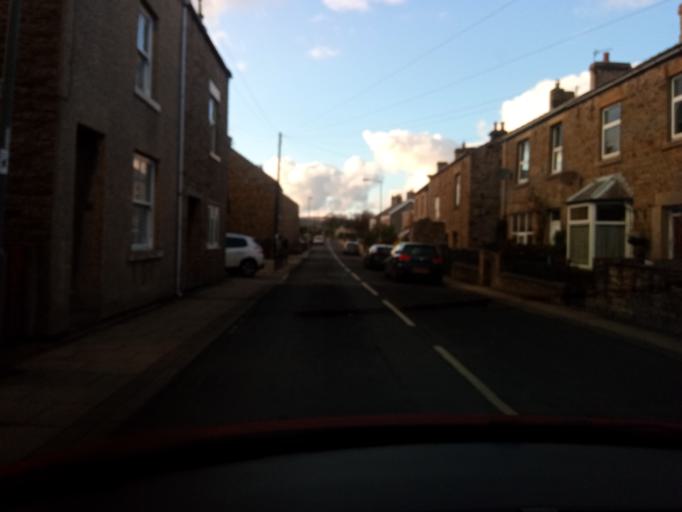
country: GB
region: England
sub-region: County Durham
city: Newbiggin
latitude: 54.7373
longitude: -2.1829
